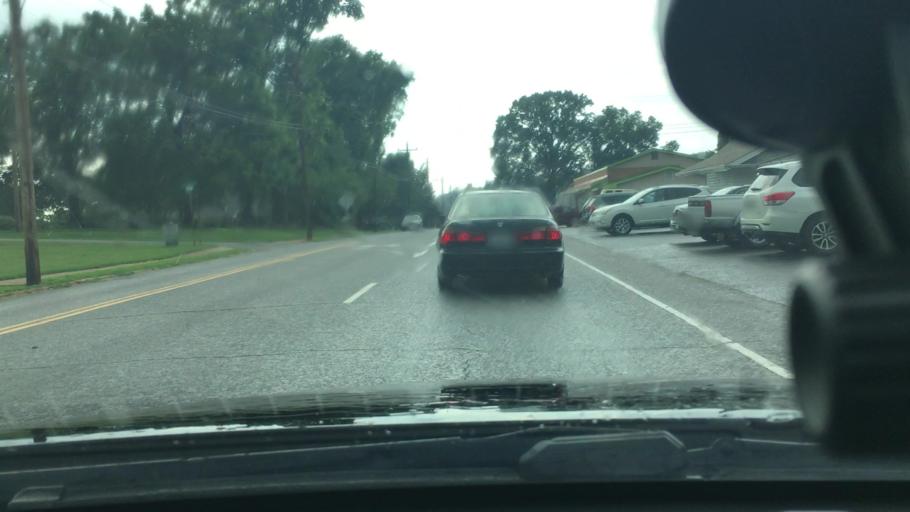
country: US
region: North Carolina
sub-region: Rutherford County
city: Spindale
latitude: 35.3598
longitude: -81.9360
